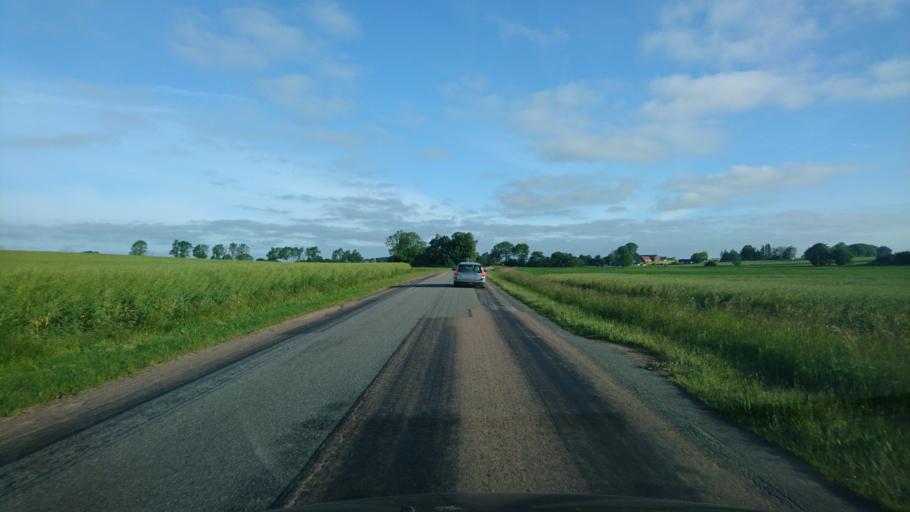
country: SE
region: Skane
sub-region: Ystads Kommun
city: Kopingebro
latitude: 55.4555
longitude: 14.1121
